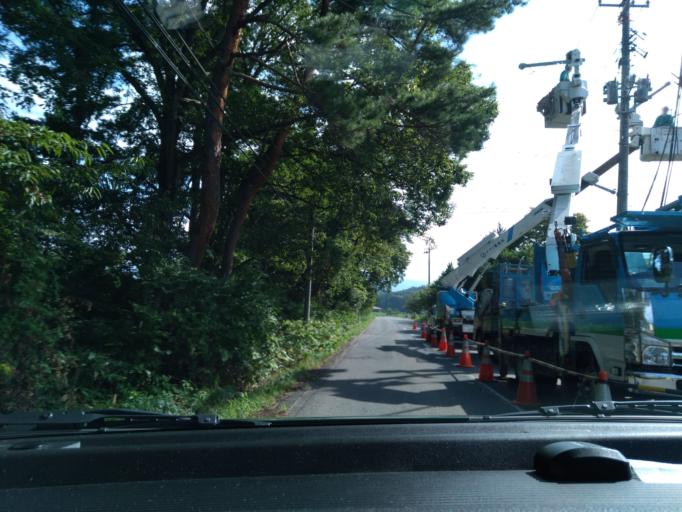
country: JP
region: Iwate
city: Shizukuishi
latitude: 39.6575
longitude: 140.9924
